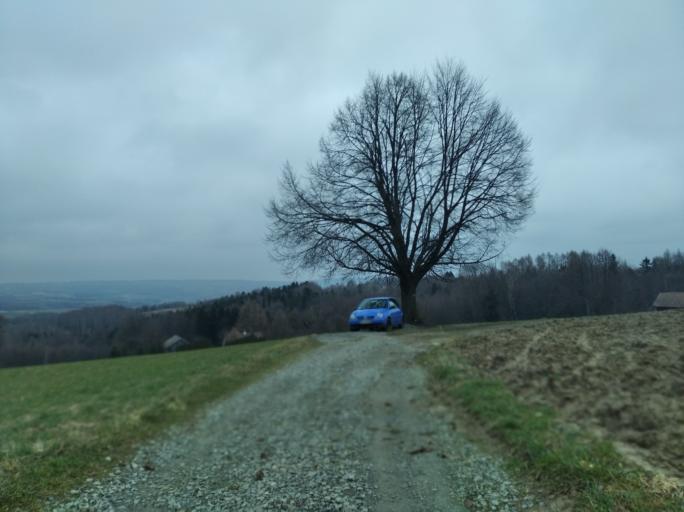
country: PL
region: Subcarpathian Voivodeship
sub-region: Powiat strzyzowski
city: Strzyzow
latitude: 49.9063
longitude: 21.7861
